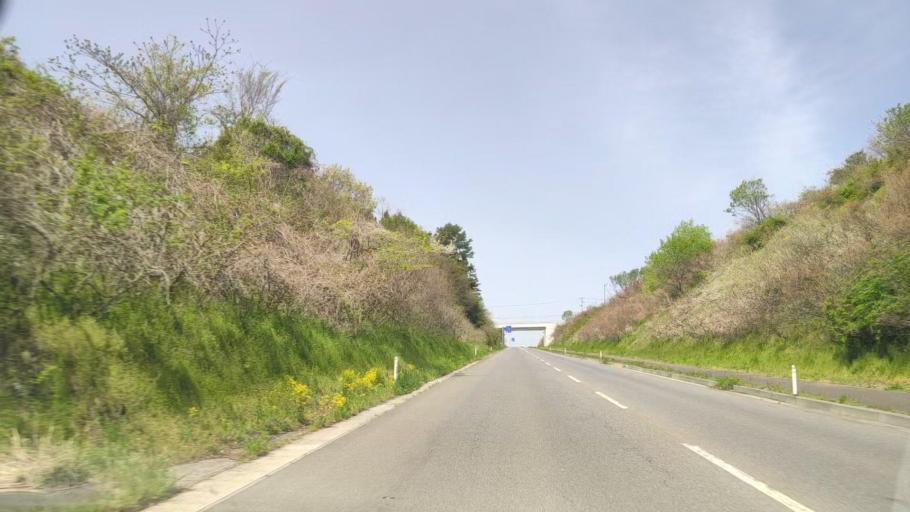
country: JP
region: Aomori
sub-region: Hachinohe Shi
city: Uchimaru
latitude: 40.5249
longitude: 141.4129
